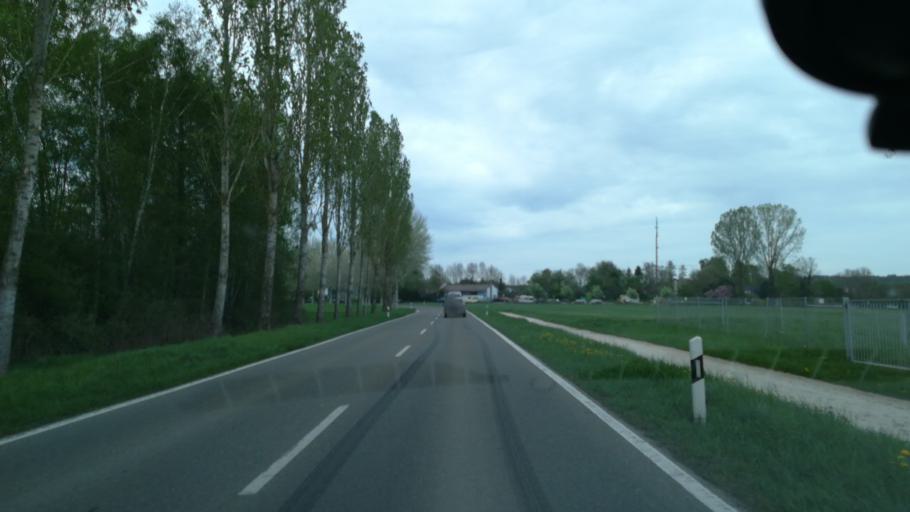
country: DE
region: Baden-Wuerttemberg
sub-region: Freiburg Region
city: Moos
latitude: 47.7455
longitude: 8.9258
